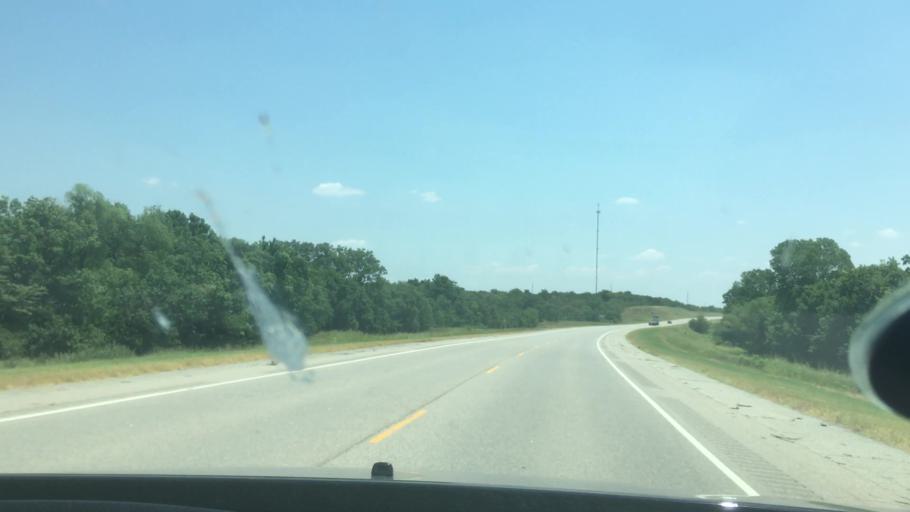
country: US
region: Oklahoma
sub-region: Pontotoc County
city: Ada
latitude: 34.6414
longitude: -96.4889
